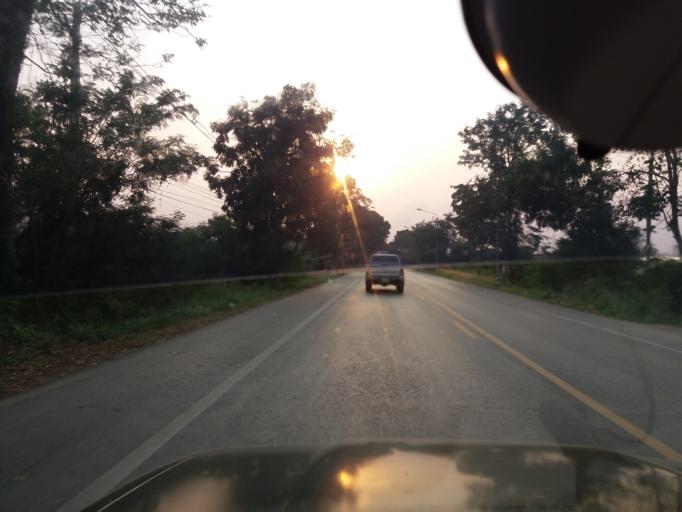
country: TH
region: Sing Buri
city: Sing Buri
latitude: 14.8845
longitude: 100.3660
